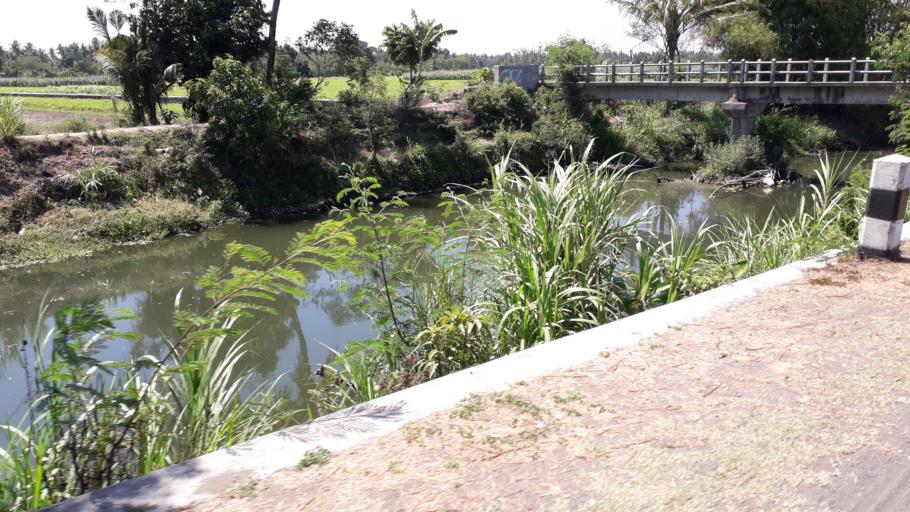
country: ID
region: Daerah Istimewa Yogyakarta
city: Pundong
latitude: -7.9474
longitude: 110.3289
